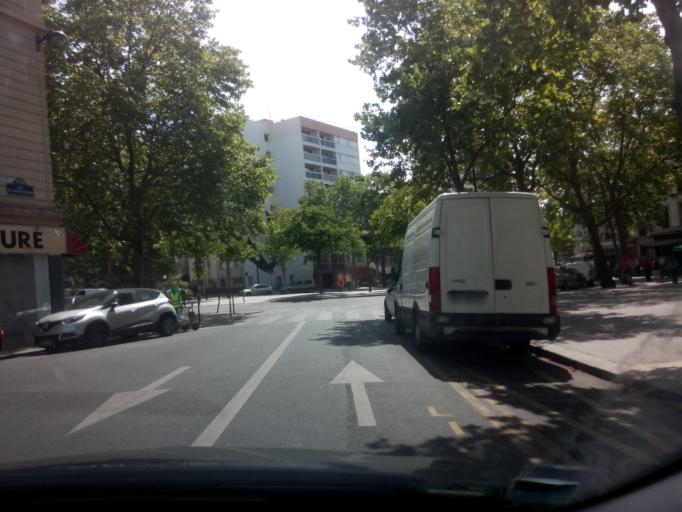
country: FR
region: Ile-de-France
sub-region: Departement du Val-de-Marne
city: Le Kremlin-Bicetre
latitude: 48.8336
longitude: 2.3608
